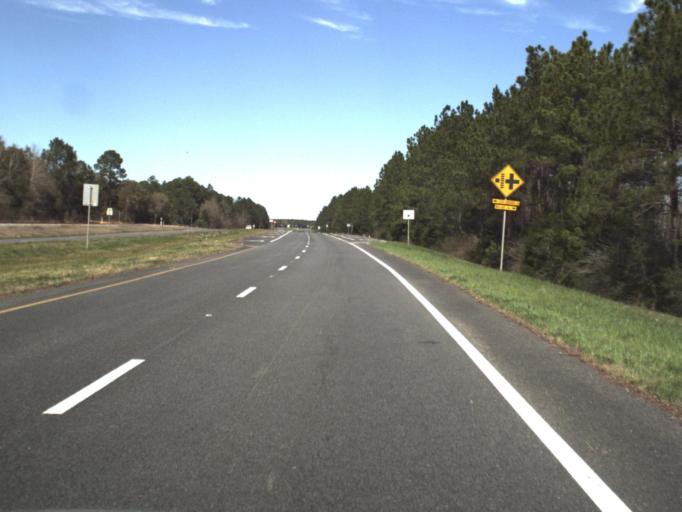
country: US
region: Florida
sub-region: Bay County
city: Youngstown
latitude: 30.5892
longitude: -85.3951
